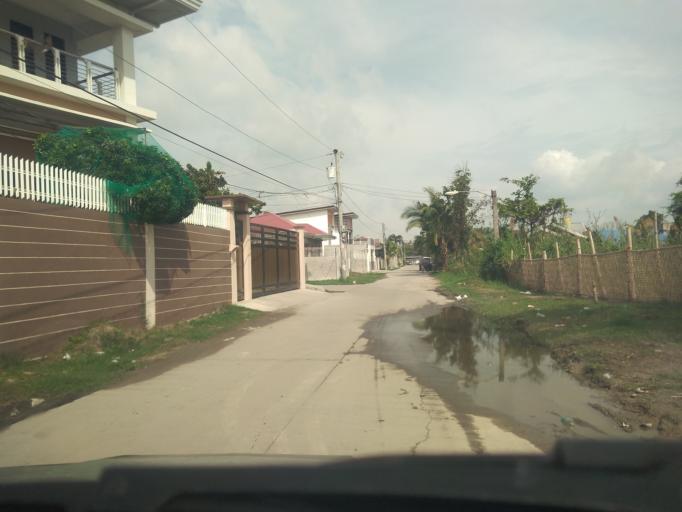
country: PH
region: Central Luzon
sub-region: Province of Pampanga
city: Pau
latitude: 15.0115
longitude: 120.7087
